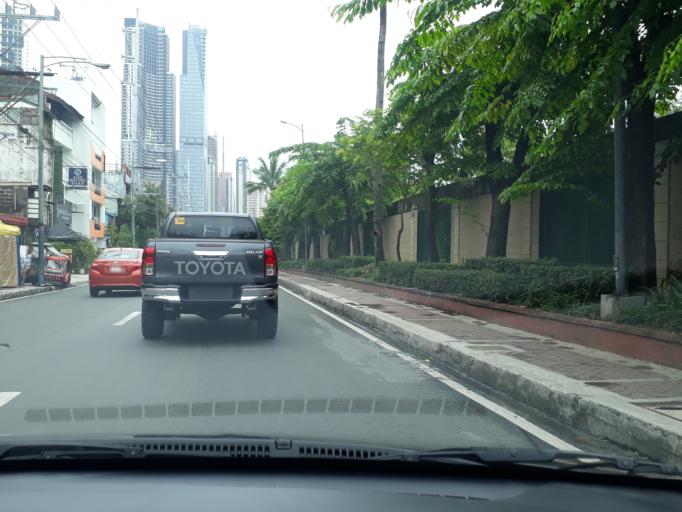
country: PH
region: Metro Manila
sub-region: Makati City
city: Makati City
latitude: 14.5676
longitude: 121.0209
